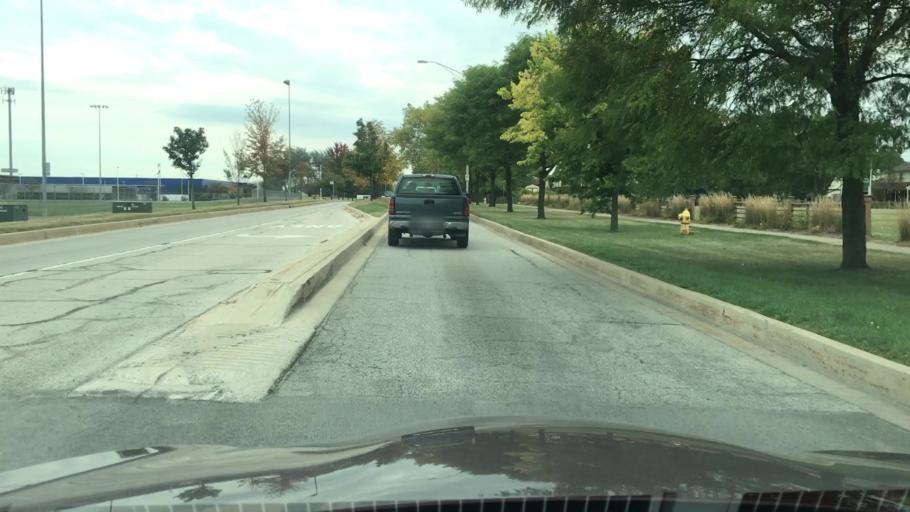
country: US
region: Illinois
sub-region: DuPage County
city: Woodridge
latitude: 41.7323
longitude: -88.0402
